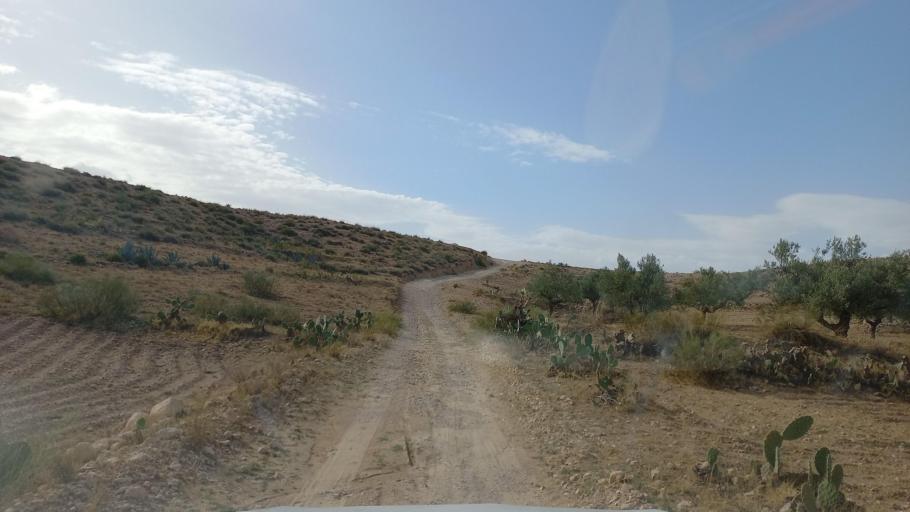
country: TN
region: Al Qasrayn
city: Kasserine
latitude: 35.2598
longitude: 8.9261
